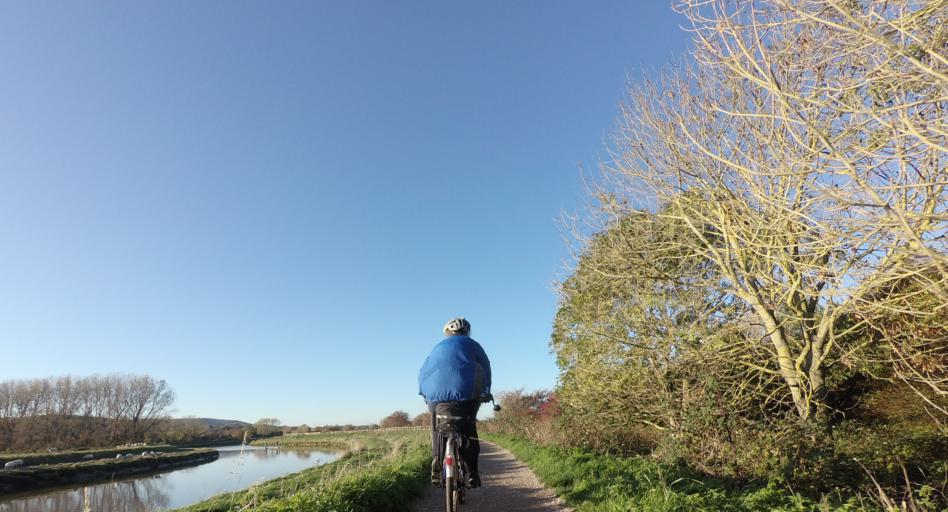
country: GB
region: England
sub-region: West Sussex
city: Steyning
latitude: 50.8684
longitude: -0.2983
